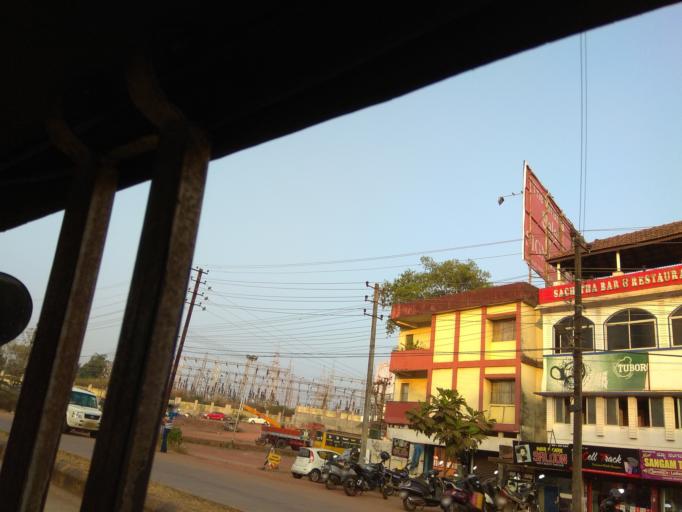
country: IN
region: Karnataka
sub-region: Dakshina Kannada
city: Mangalore
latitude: 12.9247
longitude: 74.8587
